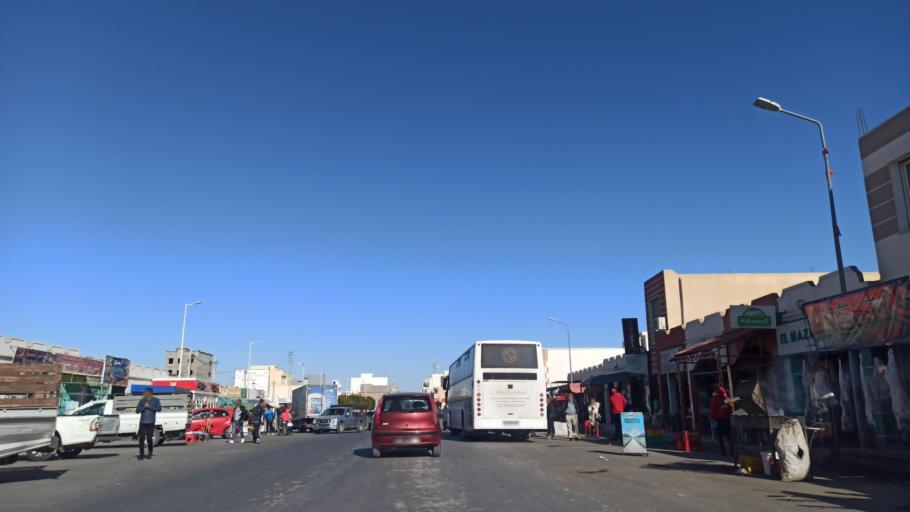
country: TN
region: Sidi Bu Zayd
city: Bi'r al Hufayy
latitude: 34.9309
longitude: 9.1949
